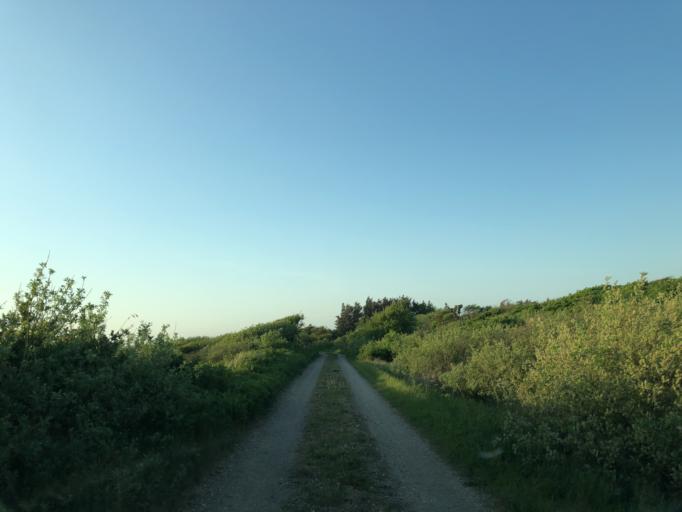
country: DK
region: Central Jutland
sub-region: Ringkobing-Skjern Kommune
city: Ringkobing
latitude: 56.2267
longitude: 8.1673
